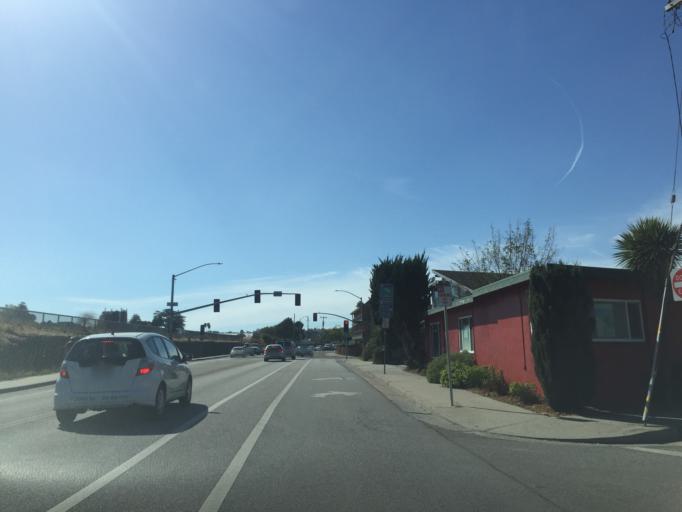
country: US
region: California
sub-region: Santa Cruz County
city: Santa Cruz
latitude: 36.9687
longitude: -122.0153
